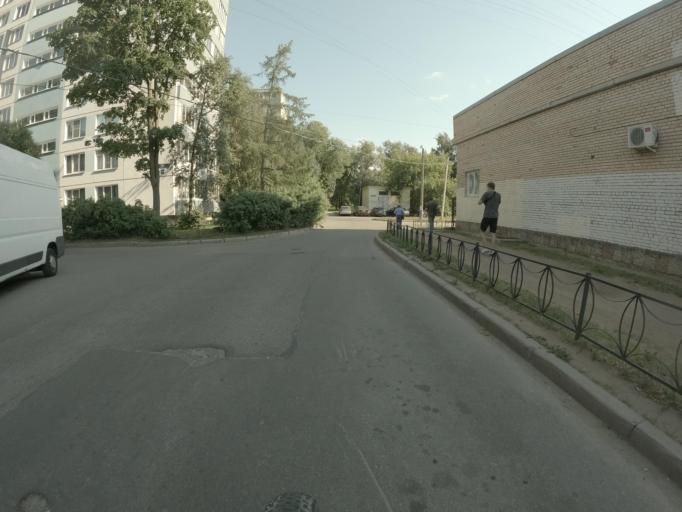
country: RU
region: St.-Petersburg
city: Kupchino
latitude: 59.8549
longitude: 30.3752
